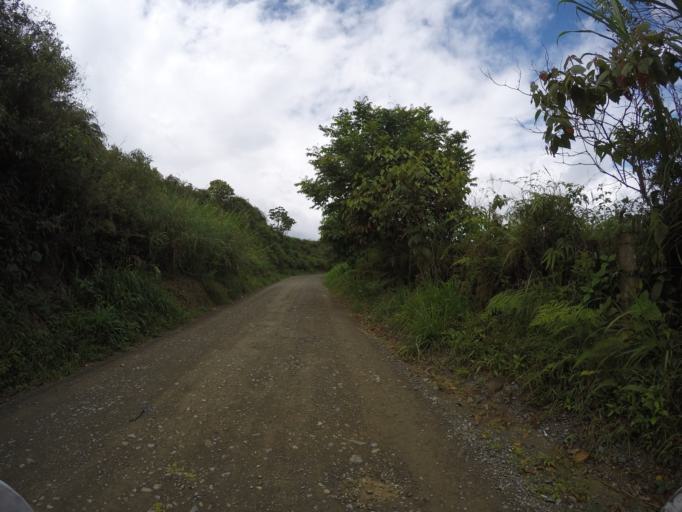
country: CO
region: Quindio
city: Filandia
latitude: 4.6652
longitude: -75.6745
